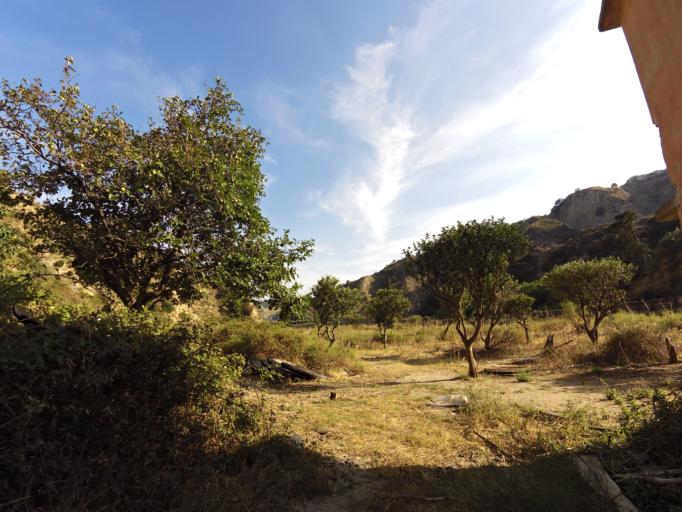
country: IT
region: Calabria
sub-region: Provincia di Reggio Calabria
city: Stilo
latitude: 38.4848
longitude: 16.4775
